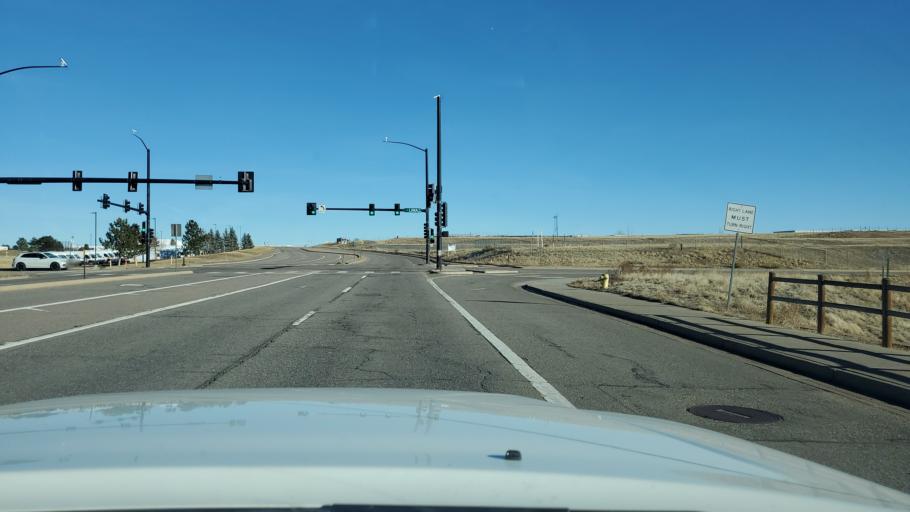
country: US
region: Colorado
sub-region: Arapahoe County
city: Centennial
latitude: 39.5875
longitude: -104.8582
